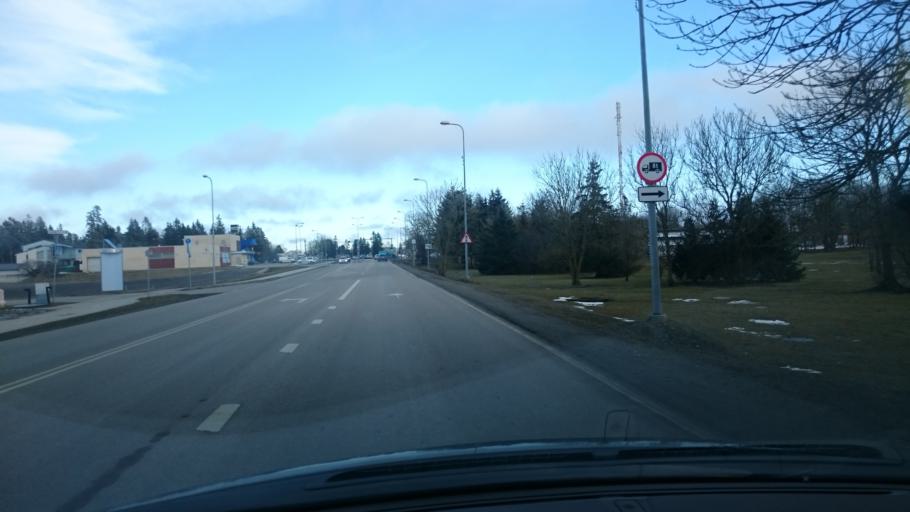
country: EE
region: Harju
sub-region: Harku vald
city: Tabasalu
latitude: 59.4296
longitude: 24.5439
